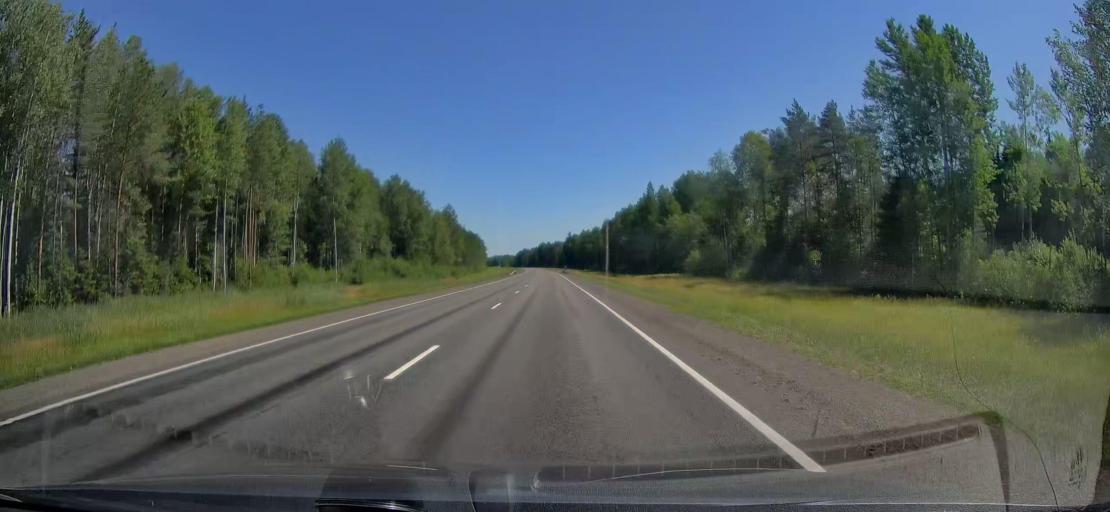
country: RU
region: Tverskaya
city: Ves'yegonsk
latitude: 58.9217
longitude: 37.2002
